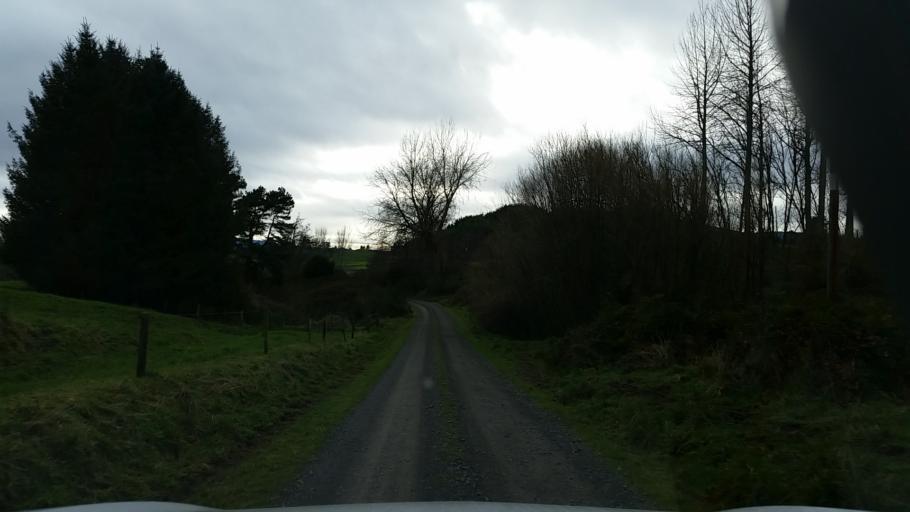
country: NZ
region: Bay of Plenty
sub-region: Rotorua District
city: Rotorua
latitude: -38.3011
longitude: 176.4211
